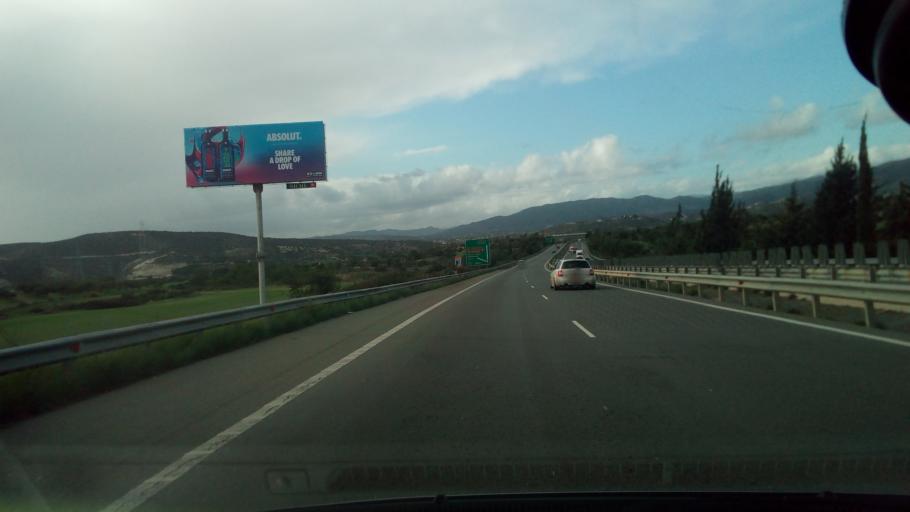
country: CY
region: Limassol
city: Pyrgos
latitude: 34.7255
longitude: 33.2451
